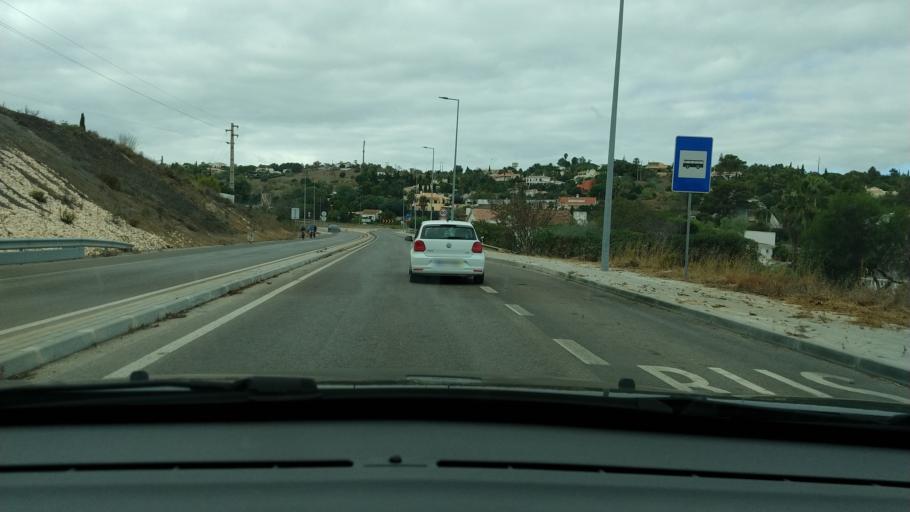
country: PT
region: Faro
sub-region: Lagos
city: Lagos
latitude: 37.1061
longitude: -8.7053
